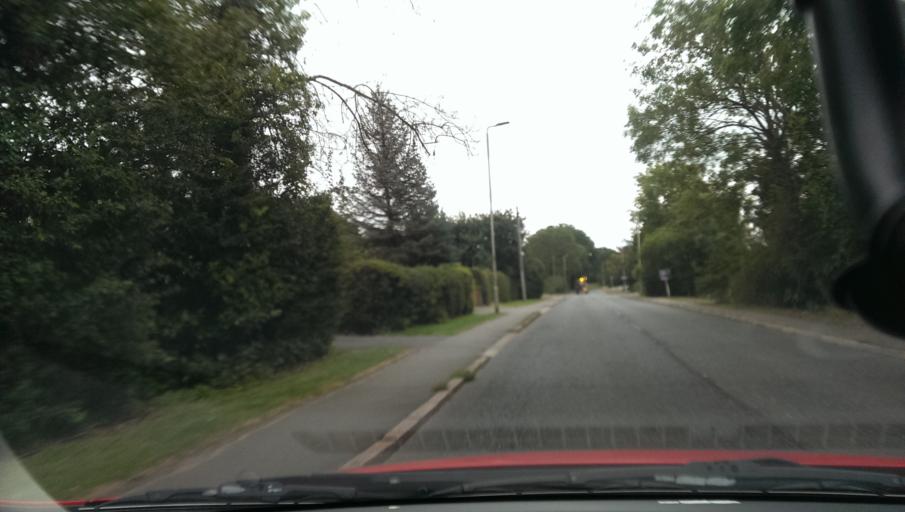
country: GB
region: England
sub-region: Leicestershire
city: Wigston Magna
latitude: 52.5801
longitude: -1.0971
